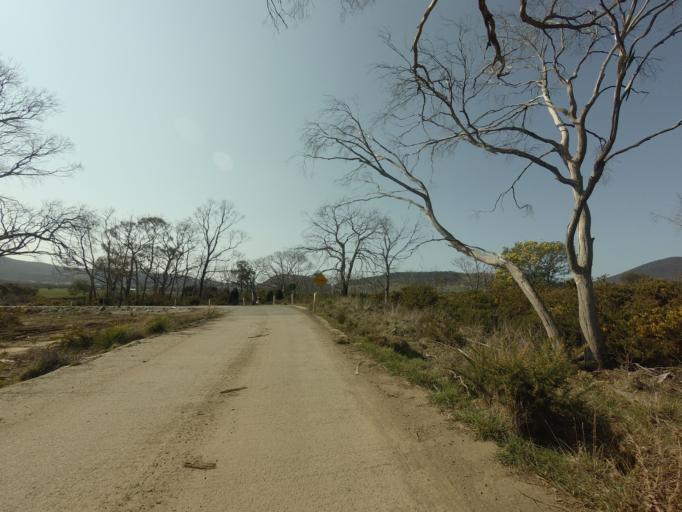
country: AU
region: Tasmania
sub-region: Break O'Day
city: St Helens
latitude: -41.8153
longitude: 147.9413
